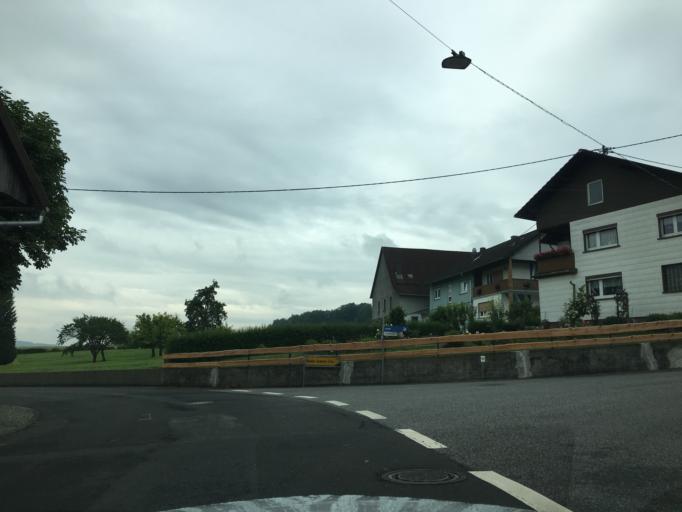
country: DE
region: Hesse
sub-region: Regierungsbezirk Darmstadt
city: Birstein
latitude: 50.3987
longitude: 9.2713
